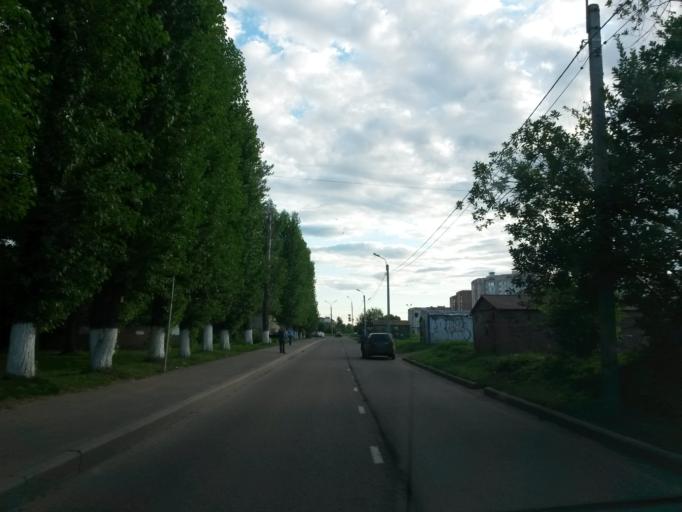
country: RU
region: Jaroslavl
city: Yaroslavl
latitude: 57.6855
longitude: 39.7712
